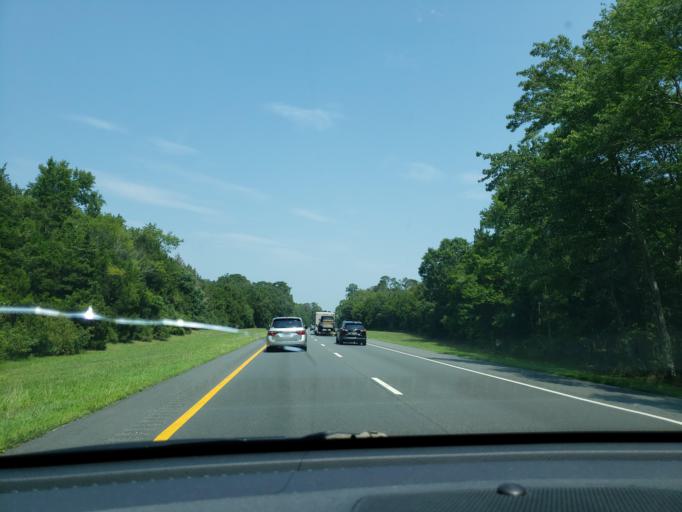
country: US
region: New Jersey
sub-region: Cape May County
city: Avalon
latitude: 39.1442
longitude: -74.7588
